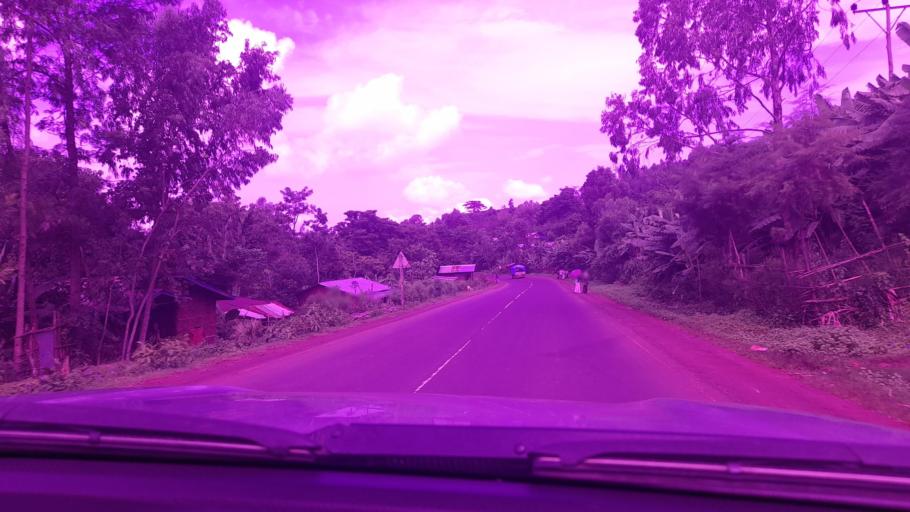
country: ET
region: Southern Nations, Nationalities, and People's Region
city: Bonga
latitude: 7.5004
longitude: 36.5001
